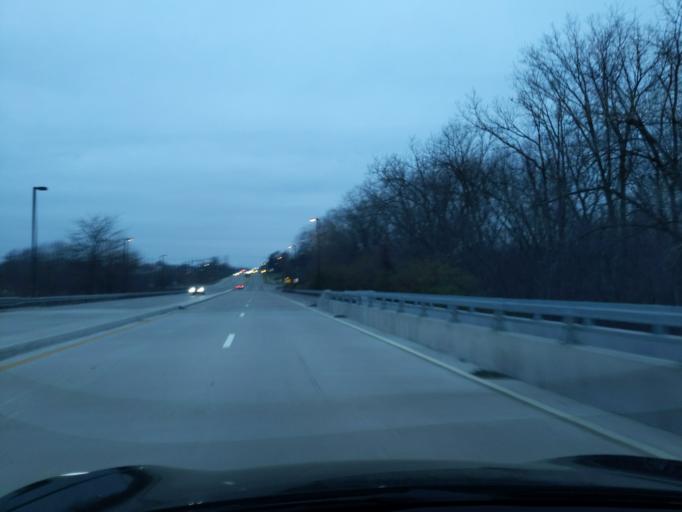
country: US
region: Indiana
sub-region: Saint Joseph County
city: Notre Dame
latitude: 41.7231
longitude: -86.2677
